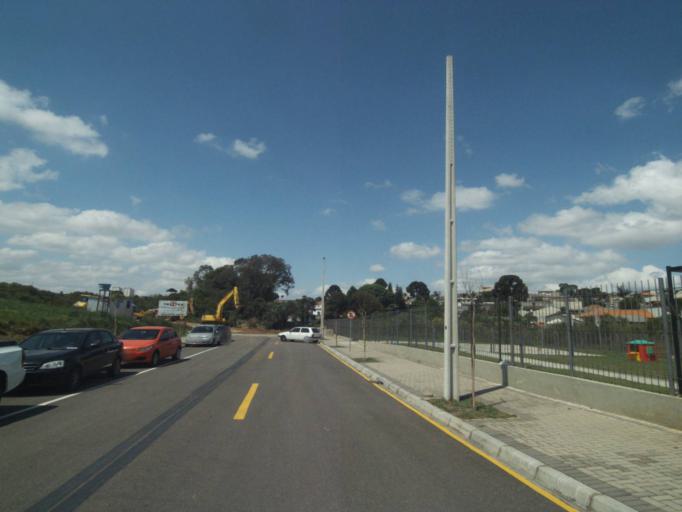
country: BR
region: Parana
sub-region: Curitiba
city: Curitiba
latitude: -25.5107
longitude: -49.3083
